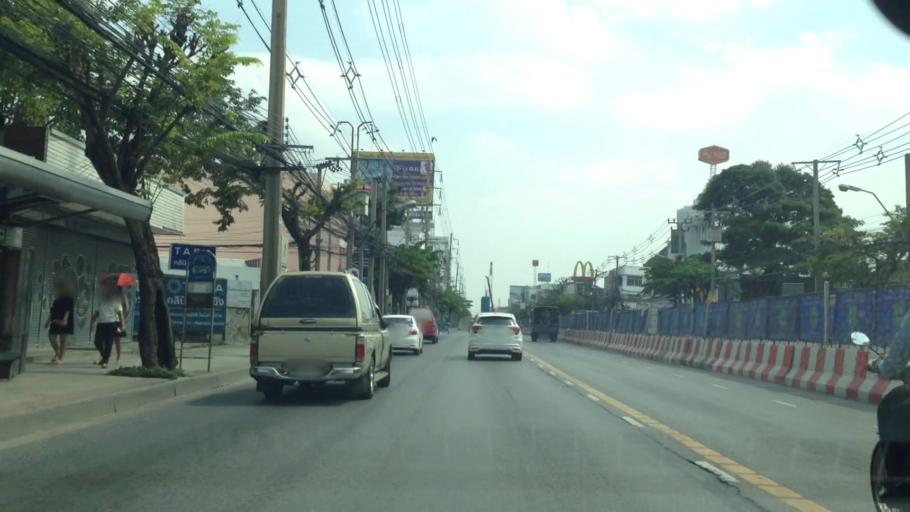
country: TH
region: Bangkok
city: Wang Thonglang
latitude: 13.7809
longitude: 100.6189
